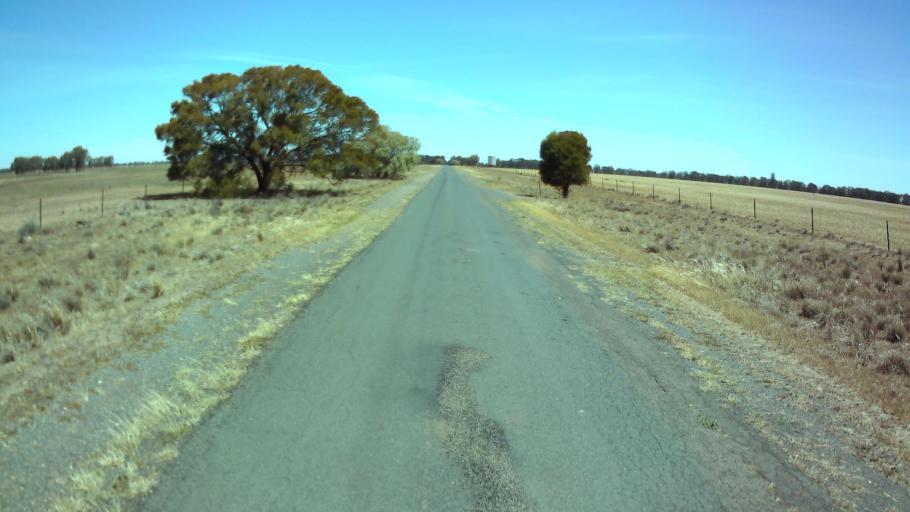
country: AU
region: New South Wales
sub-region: Weddin
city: Grenfell
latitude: -33.8553
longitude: 147.6948
